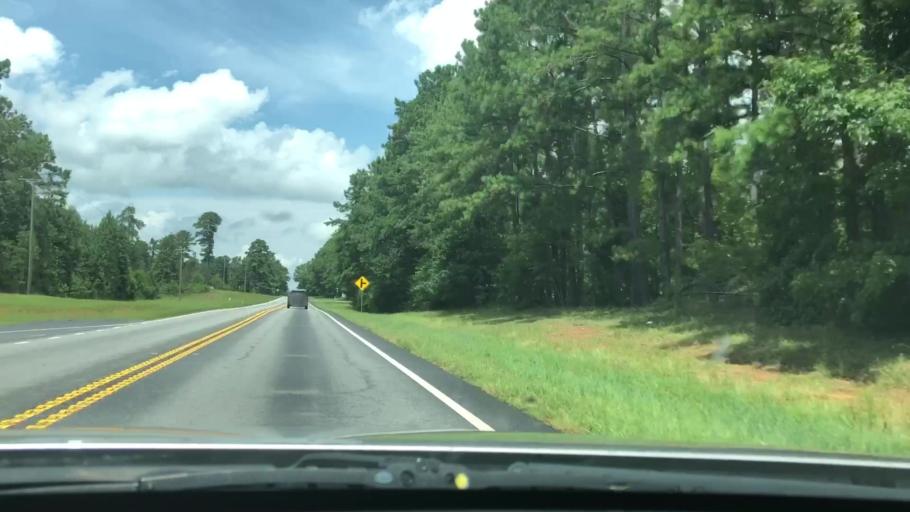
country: US
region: Georgia
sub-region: Lamar County
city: Barnesville
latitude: 33.1110
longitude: -84.1544
